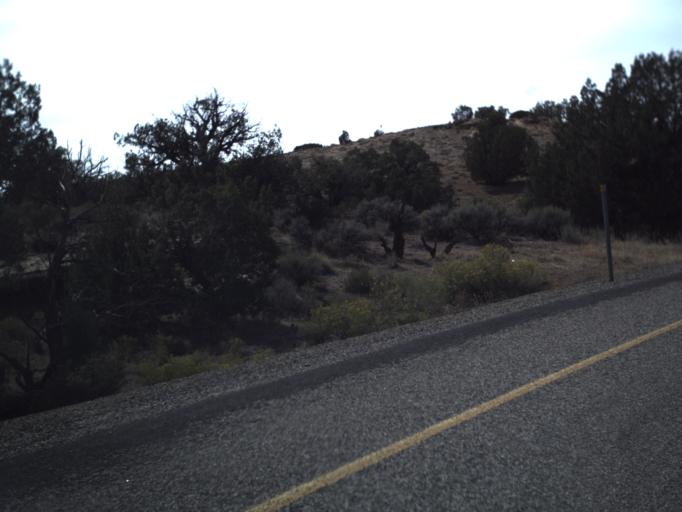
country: US
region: Colorado
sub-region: Mesa County
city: Loma
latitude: 39.1884
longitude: -109.1151
